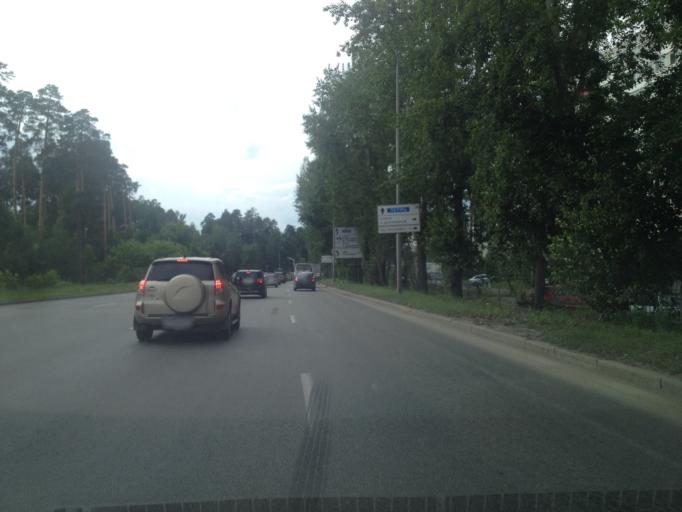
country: RU
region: Sverdlovsk
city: Sovkhoznyy
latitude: 56.8028
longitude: 60.5444
